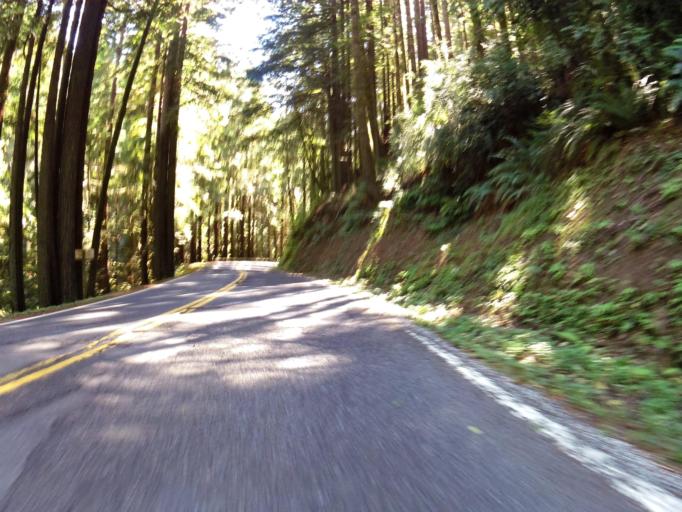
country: US
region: California
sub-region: Humboldt County
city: Redway
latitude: 39.7953
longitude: -123.8174
